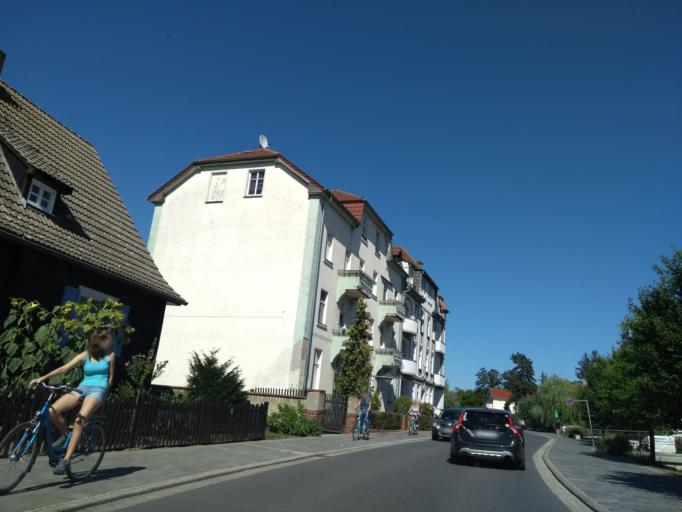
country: DE
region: Brandenburg
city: Lubbenau
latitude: 51.8640
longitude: 13.9700
